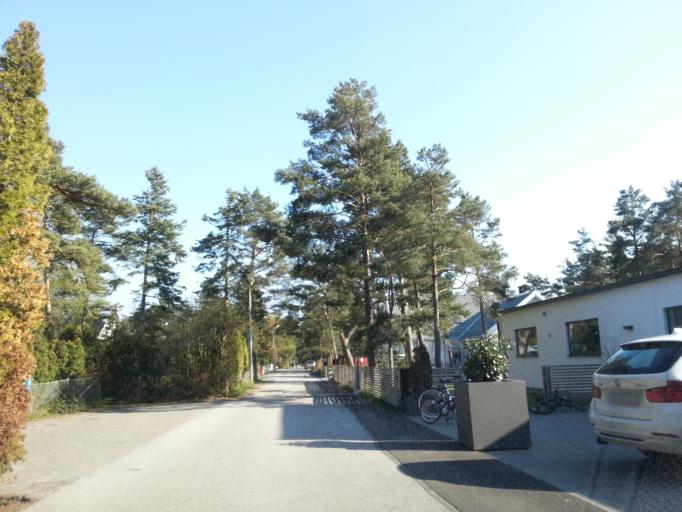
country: SE
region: Skane
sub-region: Vellinge Kommun
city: Hollviken
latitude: 55.4093
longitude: 12.9516
